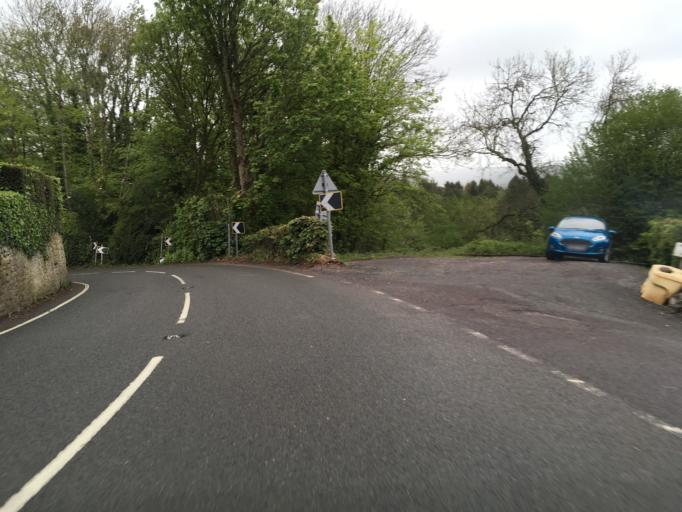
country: GB
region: England
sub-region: North Somerset
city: Blagdon
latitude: 51.3305
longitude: -2.7206
